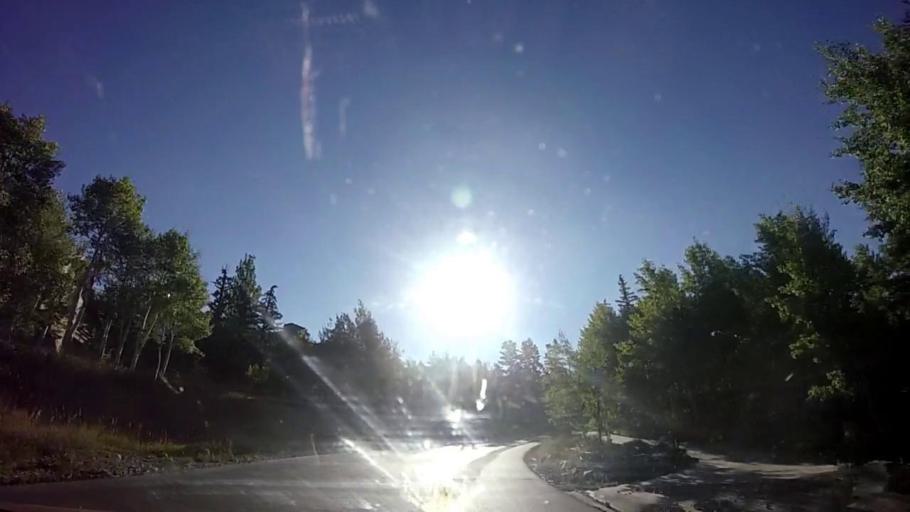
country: US
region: Utah
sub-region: Summit County
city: Park City
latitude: 40.6240
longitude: -111.4926
